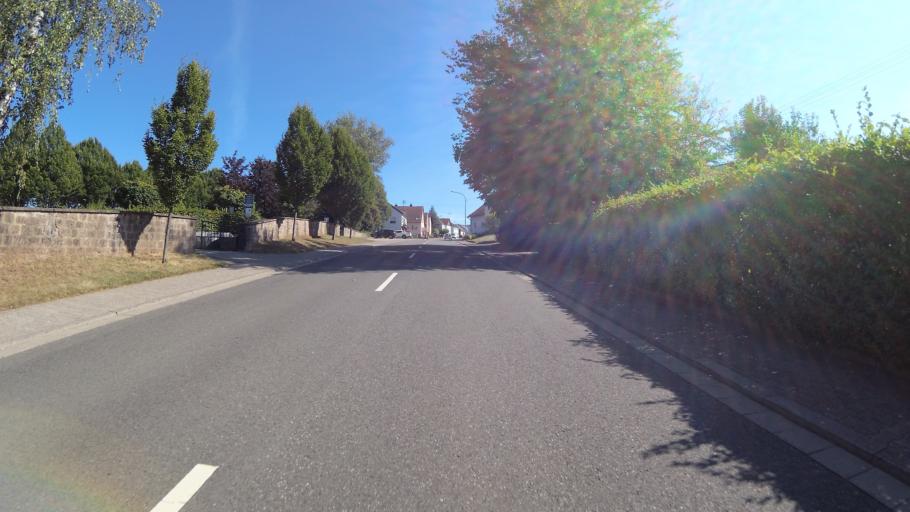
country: DE
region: Saarland
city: Eppelborn
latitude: 49.3676
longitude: 6.9821
